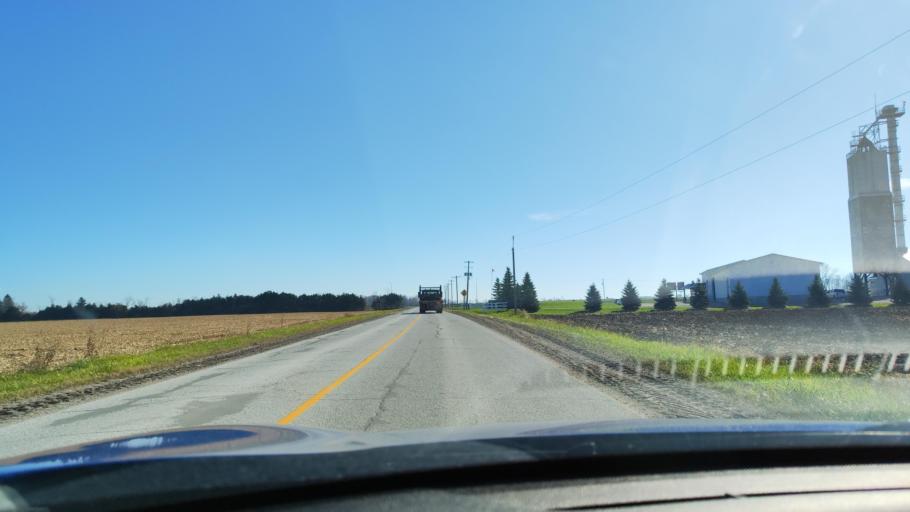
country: CA
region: Ontario
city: Wasaga Beach
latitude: 44.4396
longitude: -79.9979
